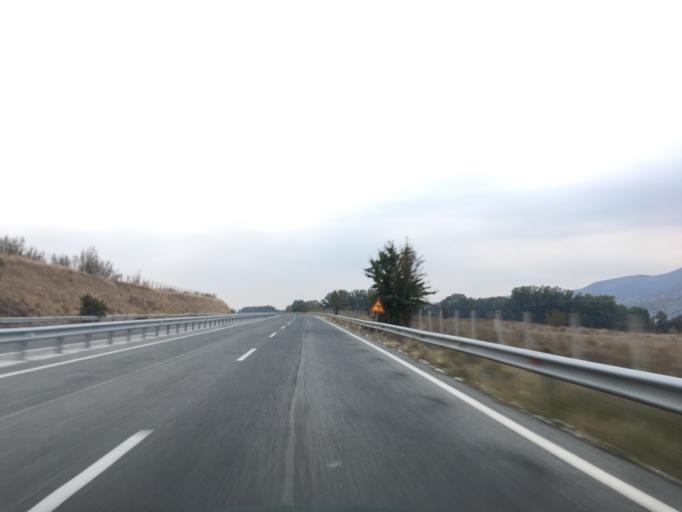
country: GR
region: Thessaly
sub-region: Trikala
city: Zarkos
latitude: 39.5875
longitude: 22.1465
